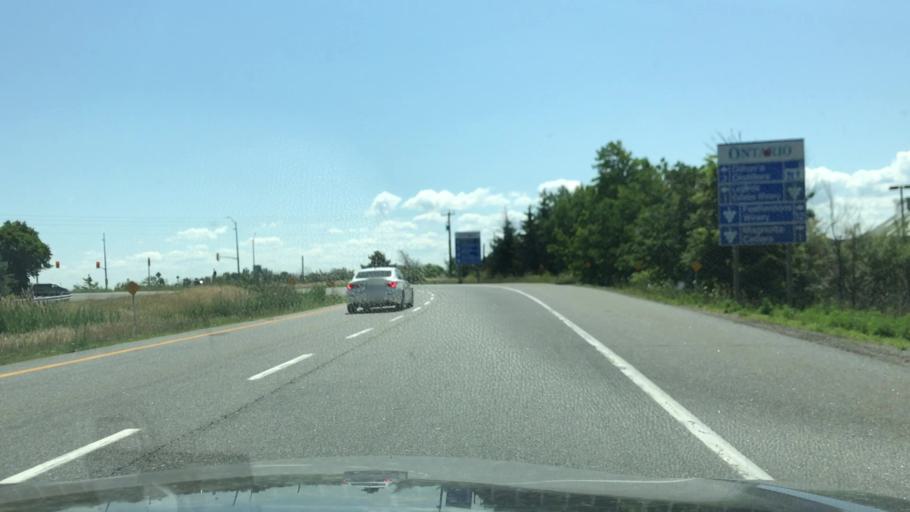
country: CA
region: Ontario
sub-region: Regional Municipality of Niagara
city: St. Catharines
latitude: 43.1882
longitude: -79.4787
